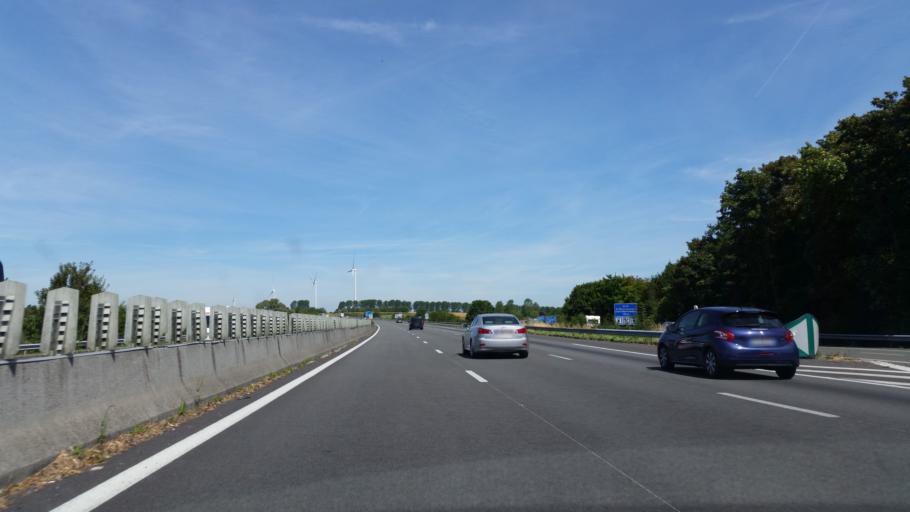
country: FR
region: Picardie
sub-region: Departement de la Somme
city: Moislains
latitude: 50.0180
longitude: 2.8820
